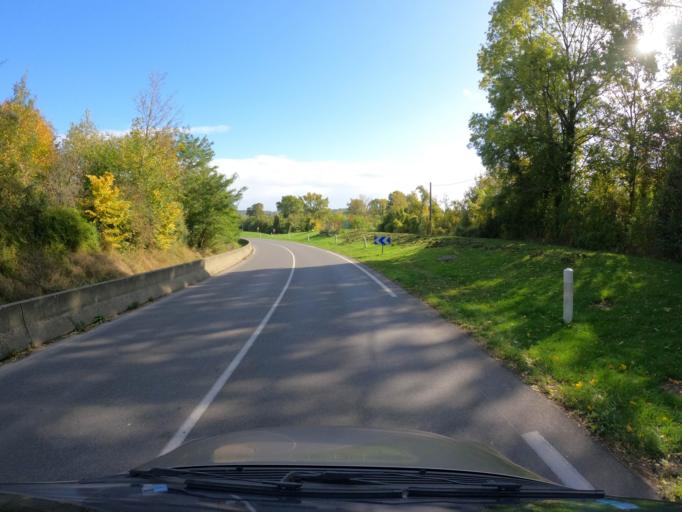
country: FR
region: Ile-de-France
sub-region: Departement de Seine-et-Marne
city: Montry
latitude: 48.8813
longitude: 2.8236
